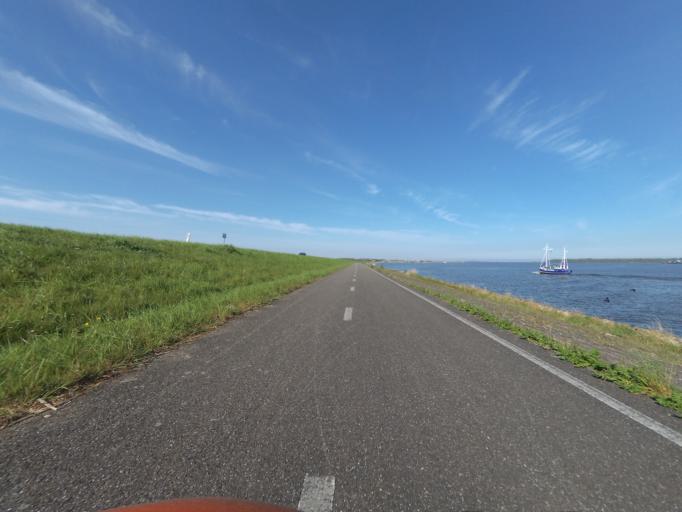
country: NL
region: Flevoland
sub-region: Gemeente Noordoostpolder
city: Ens
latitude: 52.5796
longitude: 5.7824
